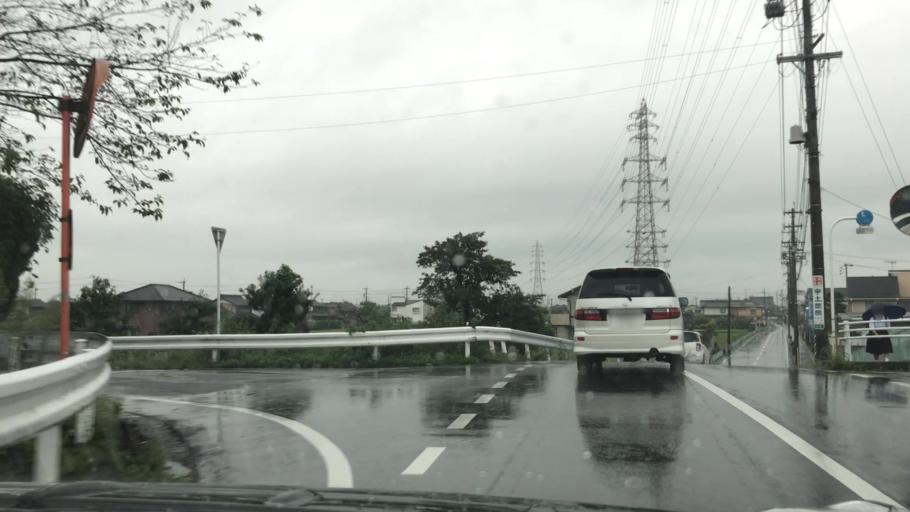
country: JP
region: Gifu
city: Gifu-shi
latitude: 35.4046
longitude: 136.6866
